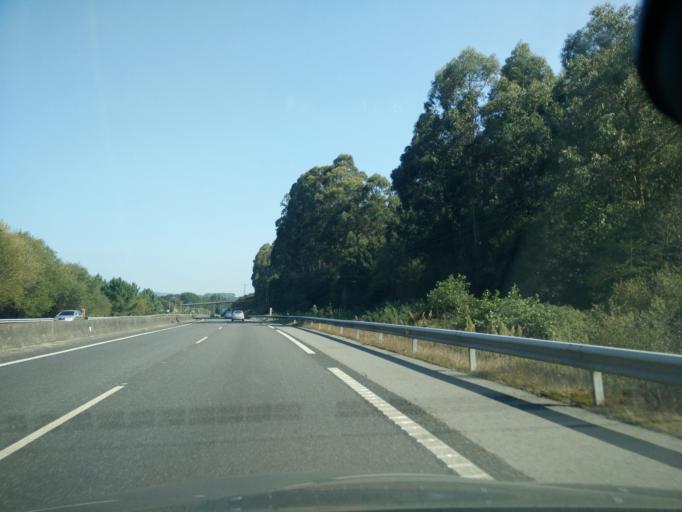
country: ES
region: Galicia
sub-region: Provincia da Coruna
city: Mino
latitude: 43.3670
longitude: -8.1950
